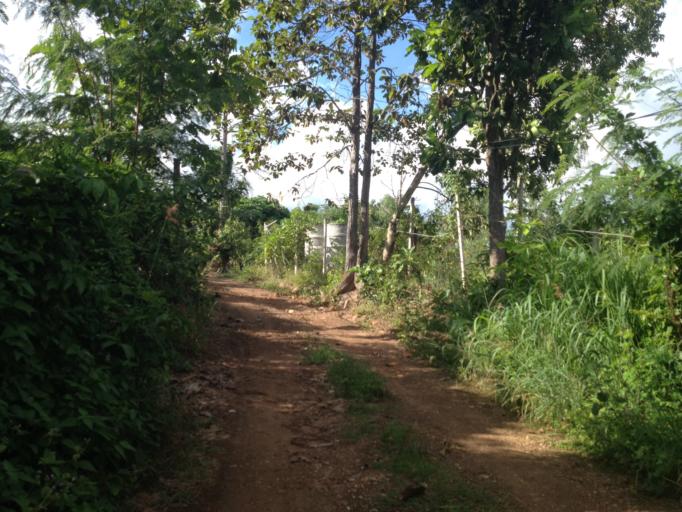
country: TH
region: Chiang Mai
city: Hang Dong
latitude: 18.7021
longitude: 98.8927
